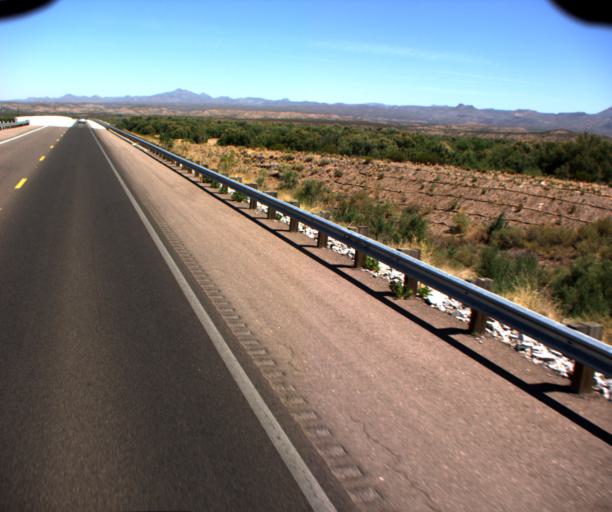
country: US
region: Arizona
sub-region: Graham County
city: Bylas
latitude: 33.1615
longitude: -110.1323
